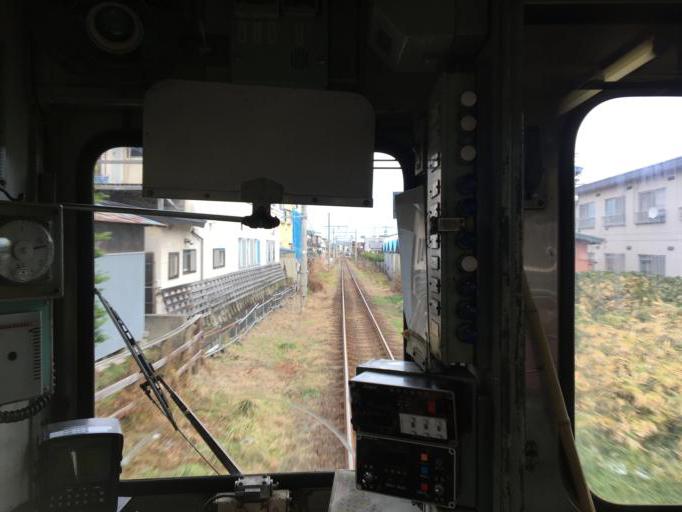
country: JP
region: Aomori
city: Hirosaki
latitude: 40.5804
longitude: 140.4717
